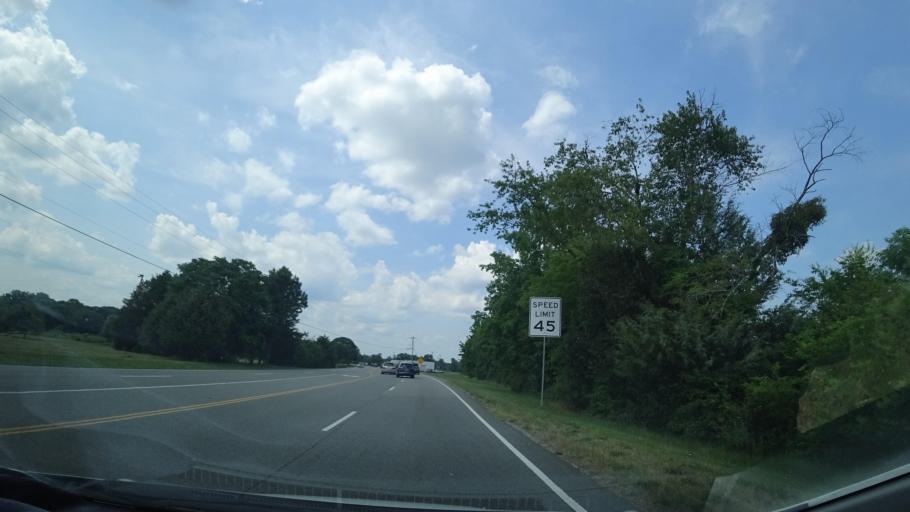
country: US
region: Virginia
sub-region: Hanover County
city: Ashland
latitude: 37.7859
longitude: -77.4658
